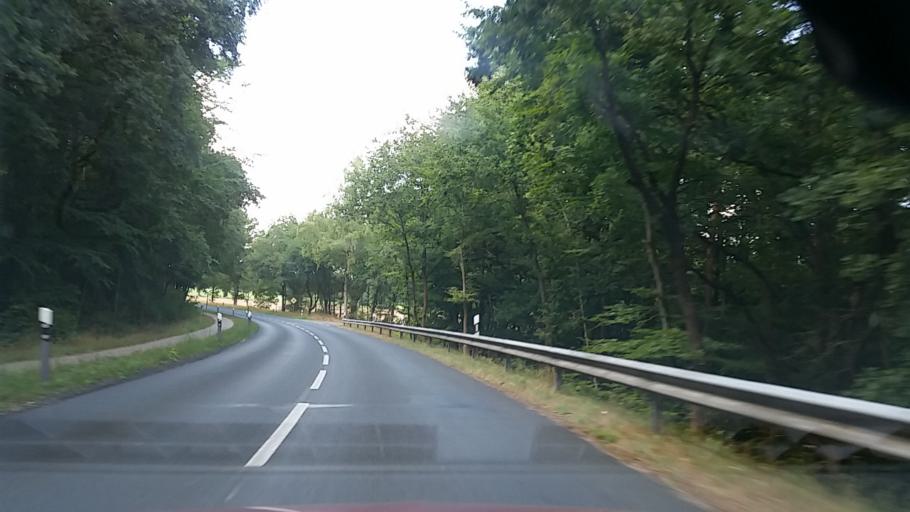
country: DE
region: Lower Saxony
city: Adendorf
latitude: 53.2961
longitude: 10.4589
